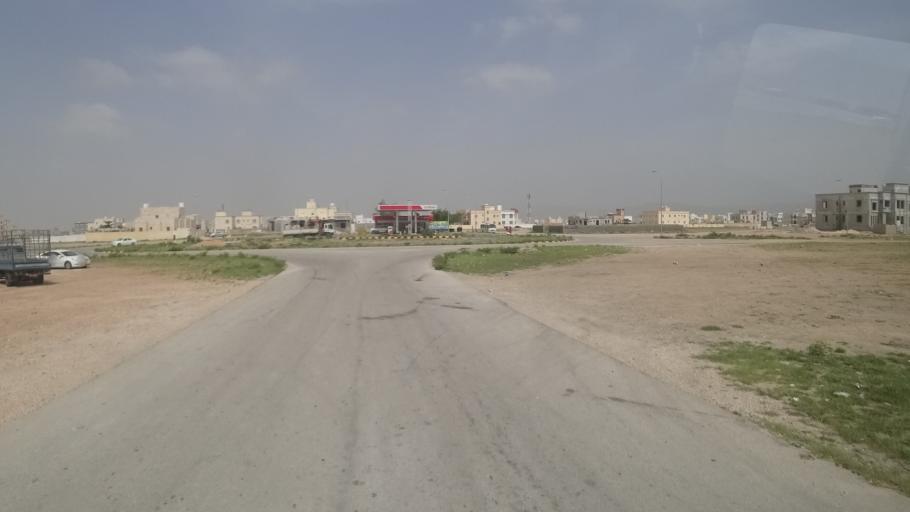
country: OM
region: Zufar
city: Salalah
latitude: 17.0975
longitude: 54.2165
